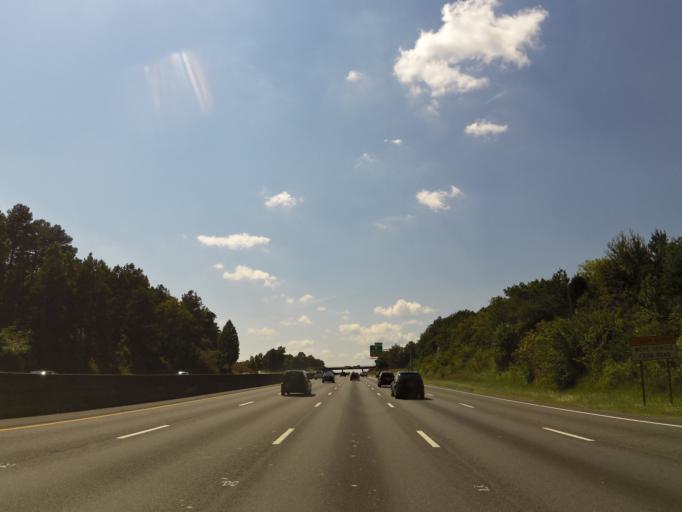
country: US
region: North Carolina
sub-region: Gaston County
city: Belmont
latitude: 35.2575
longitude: -81.0207
